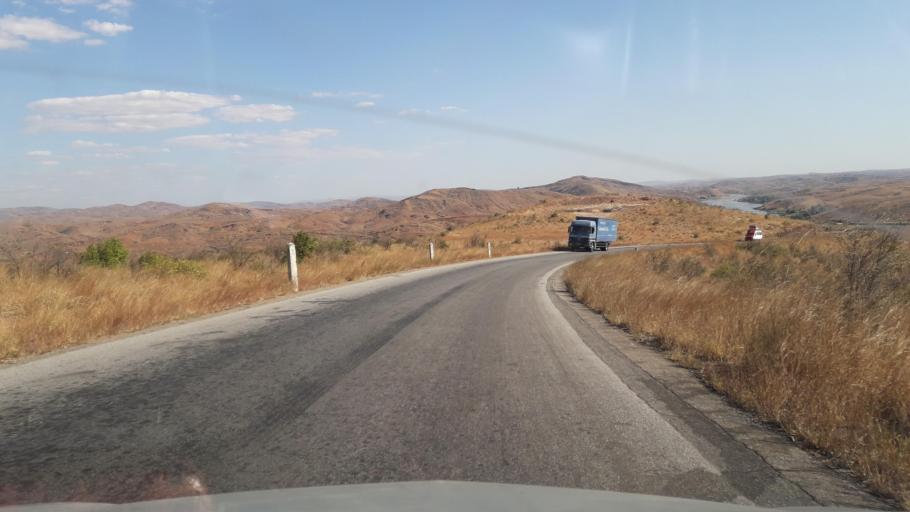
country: MG
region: Betsiboka
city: Maevatanana
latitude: -17.1707
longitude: 46.8469
